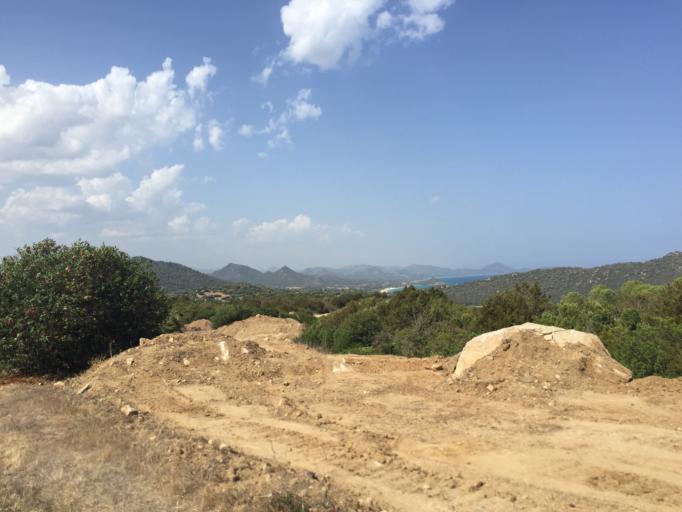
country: IT
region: Sardinia
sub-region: Provincia di Cagliari
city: Villasimius
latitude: 39.1672
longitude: 9.5612
